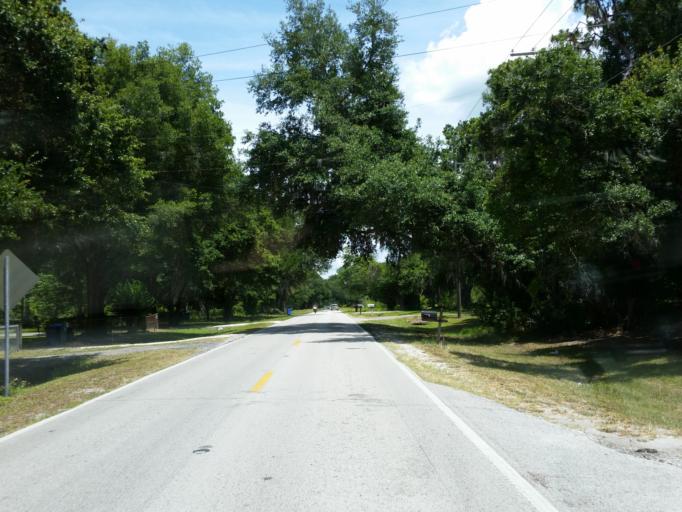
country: US
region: Florida
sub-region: Hillsborough County
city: Dover
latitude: 28.0471
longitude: -82.2348
